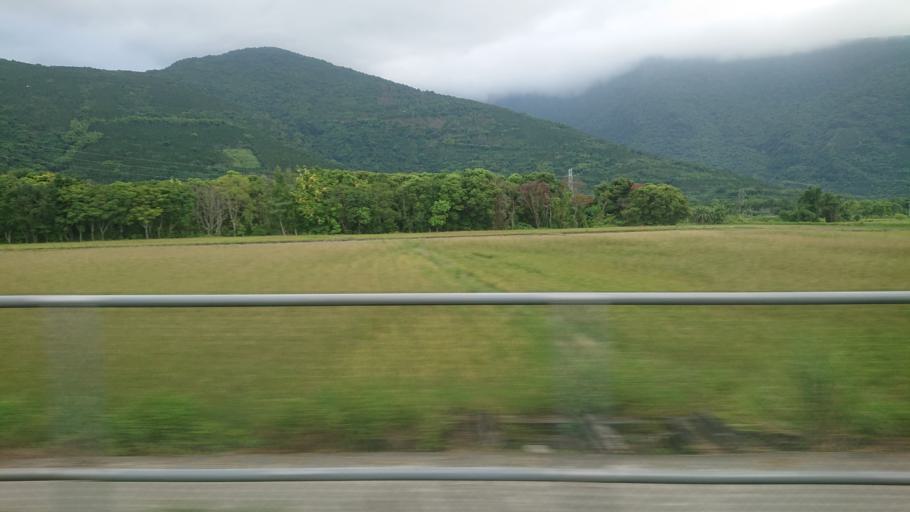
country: TW
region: Taiwan
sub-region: Hualien
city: Hualian
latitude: 23.7371
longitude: 121.4421
